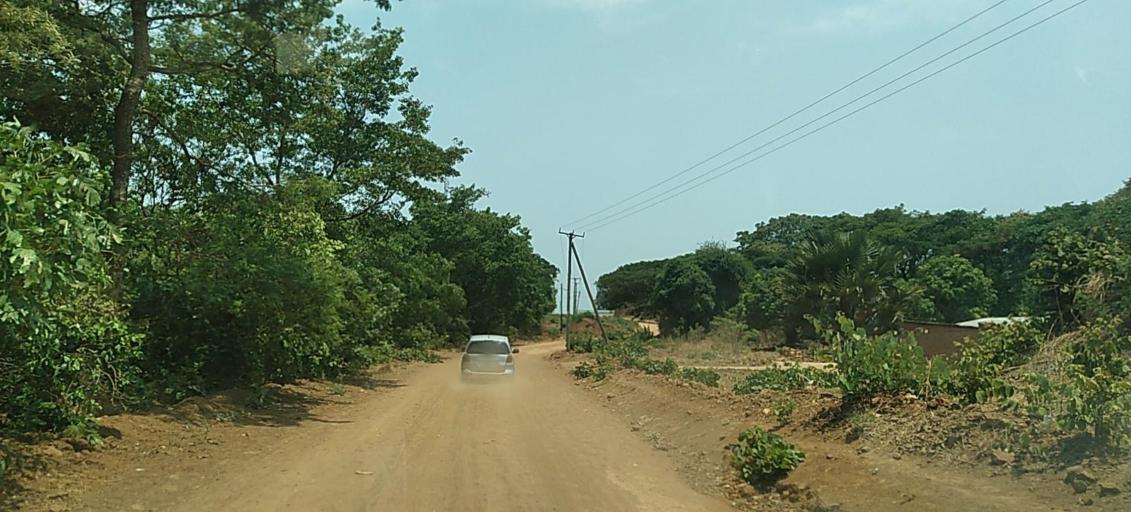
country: ZM
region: Copperbelt
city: Ndola
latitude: -13.0023
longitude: 28.7416
